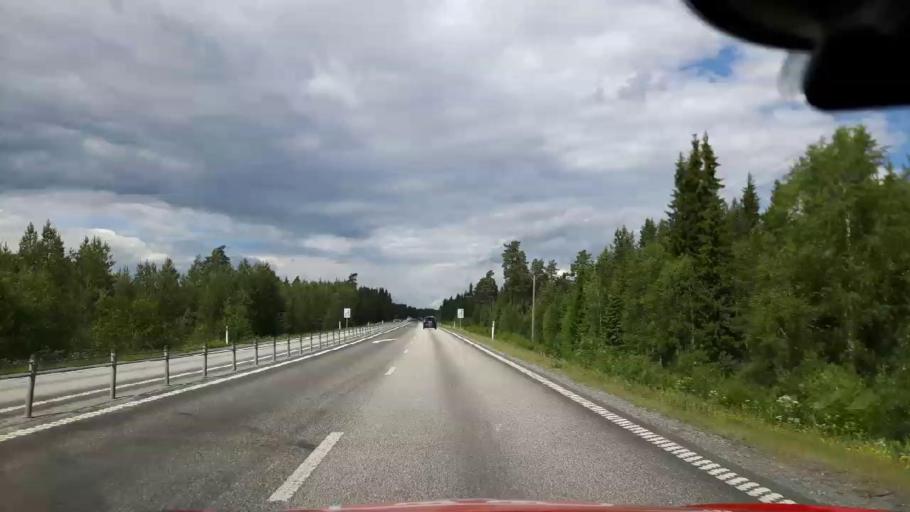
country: SE
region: Jaemtland
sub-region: OEstersunds Kommun
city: Ostersund
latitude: 63.2248
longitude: 14.6227
